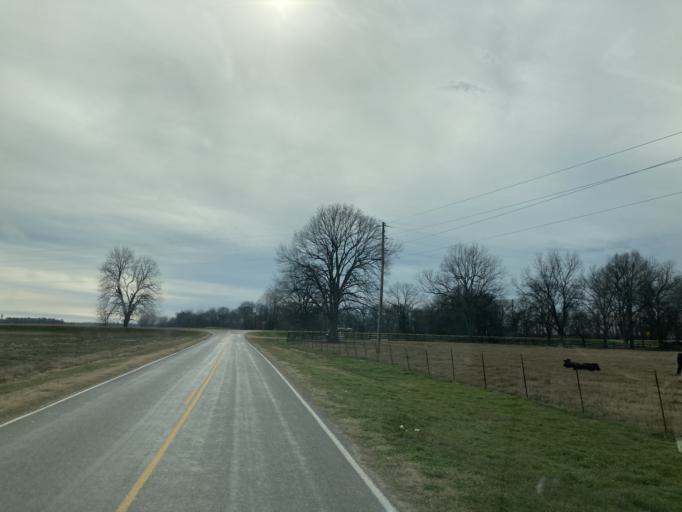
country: US
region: Mississippi
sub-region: Washington County
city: Hollandale
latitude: 33.1859
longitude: -90.6823
